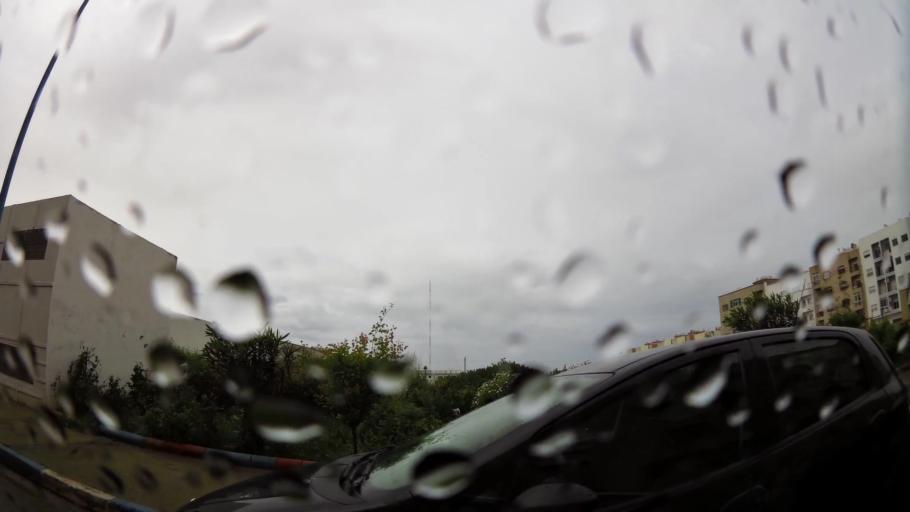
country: MA
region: Grand Casablanca
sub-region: Mediouna
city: Tit Mellil
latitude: 33.6213
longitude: -7.4867
